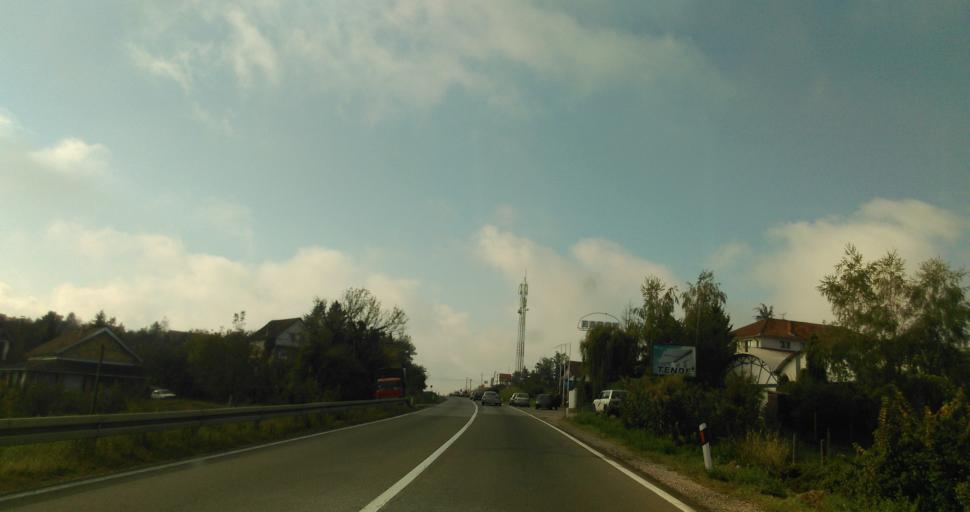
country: RS
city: Vranic
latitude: 44.6136
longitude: 20.3615
